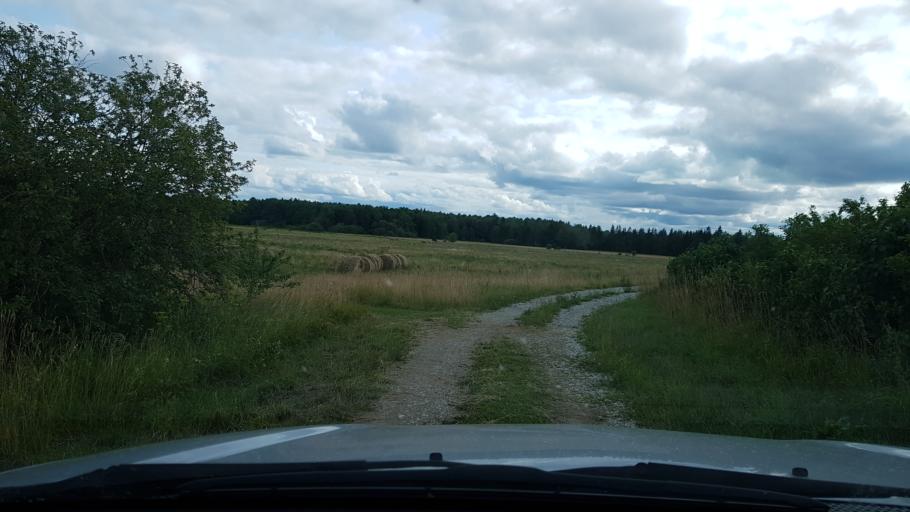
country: EE
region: Ida-Virumaa
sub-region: Narva-Joesuu linn
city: Narva-Joesuu
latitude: 59.3995
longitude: 28.0485
